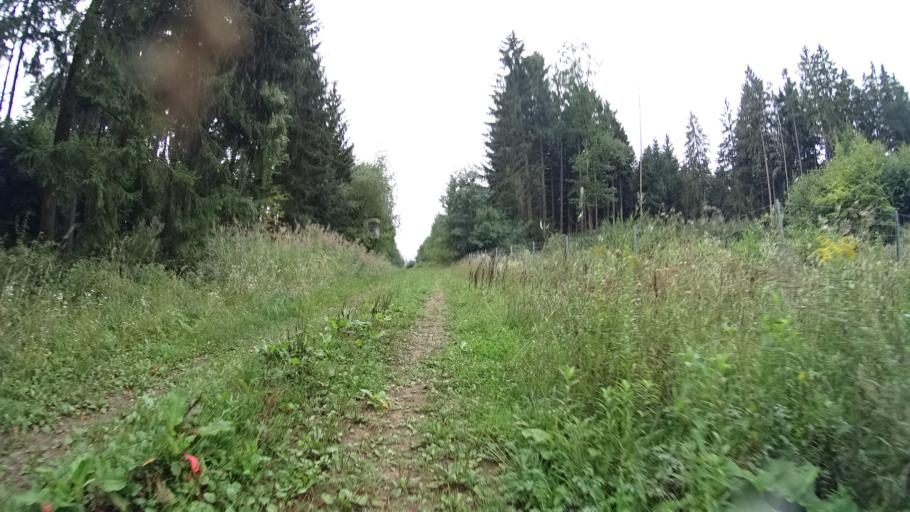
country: DE
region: Bavaria
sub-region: Upper Bavaria
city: Bohmfeld
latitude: 48.8482
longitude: 11.3566
